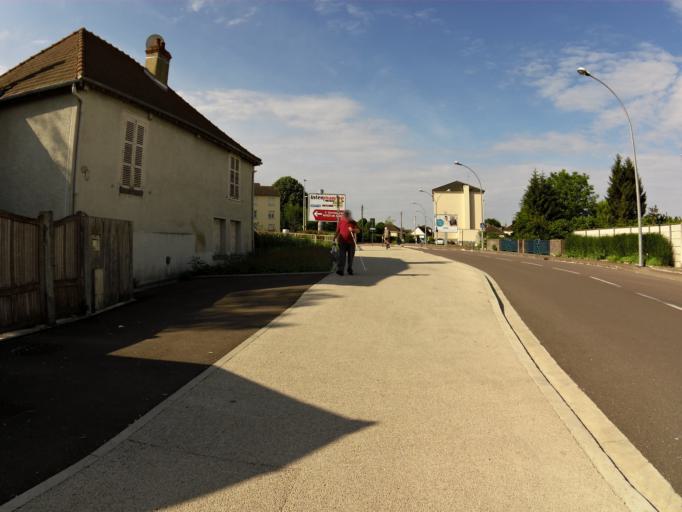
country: FR
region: Champagne-Ardenne
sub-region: Departement de l'Aube
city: Saint-Julien-les-Villas
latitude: 48.2834
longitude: 4.0923
